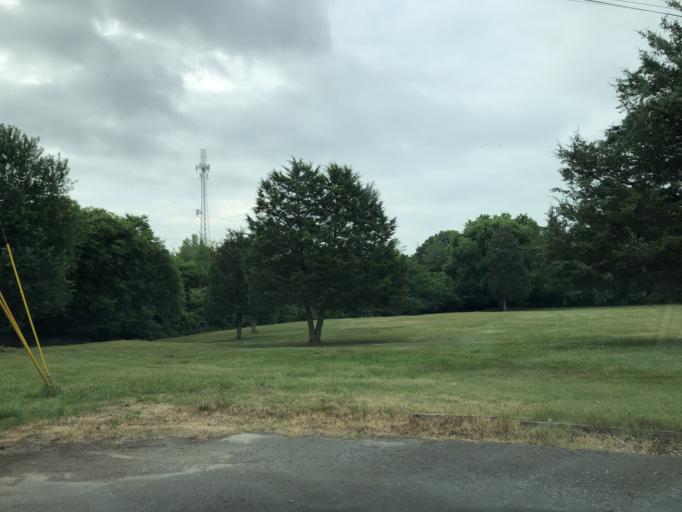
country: US
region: Tennessee
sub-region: Davidson County
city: Goodlettsville
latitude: 36.2807
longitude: -86.7166
